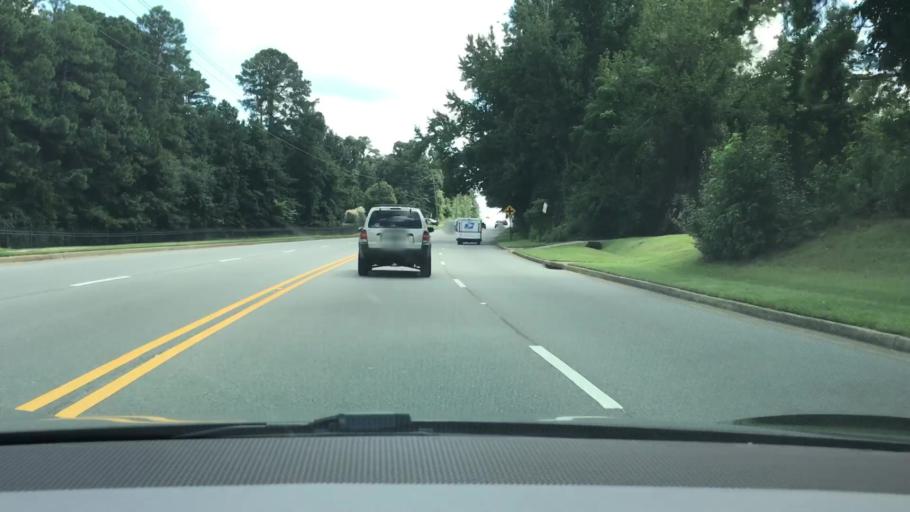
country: US
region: Alabama
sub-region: Lee County
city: Auburn
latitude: 32.6213
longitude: -85.4477
